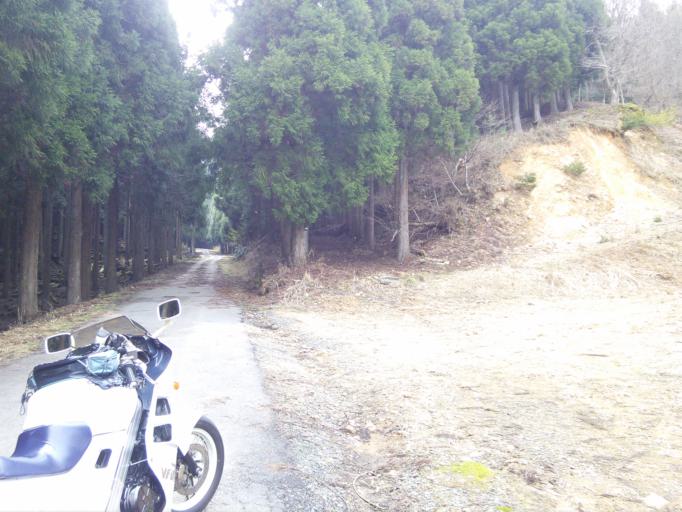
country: JP
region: Kyoto
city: Fukuchiyama
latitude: 35.3830
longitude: 135.0019
